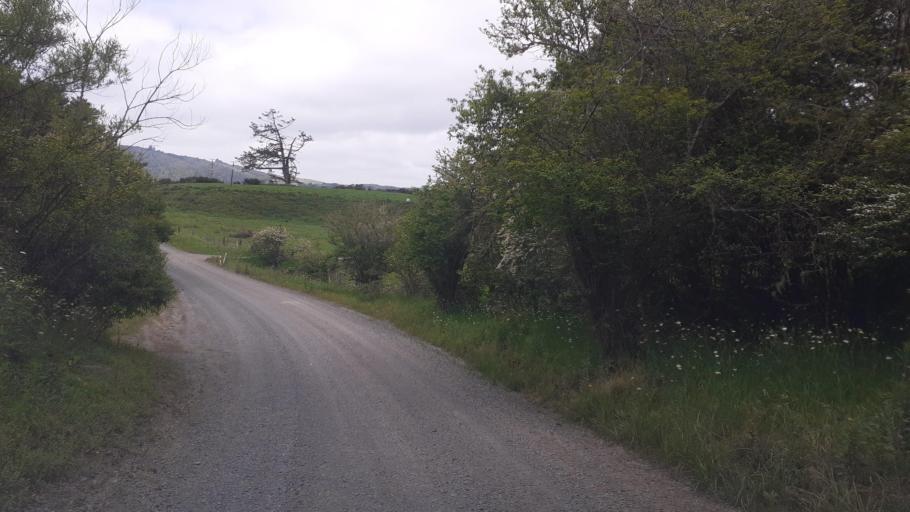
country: NZ
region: Northland
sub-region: Far North District
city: Kawakawa
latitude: -35.4151
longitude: 174.0826
